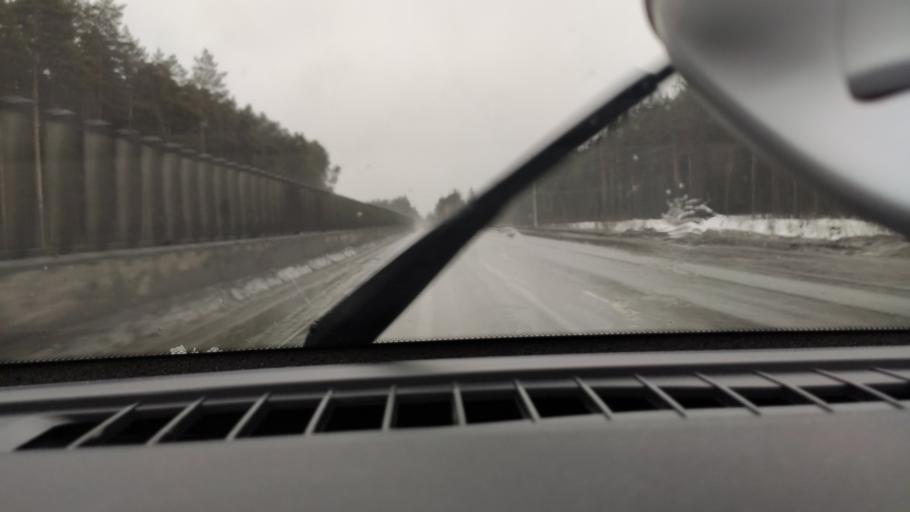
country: RU
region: Perm
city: Overyata
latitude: 58.0373
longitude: 55.9794
